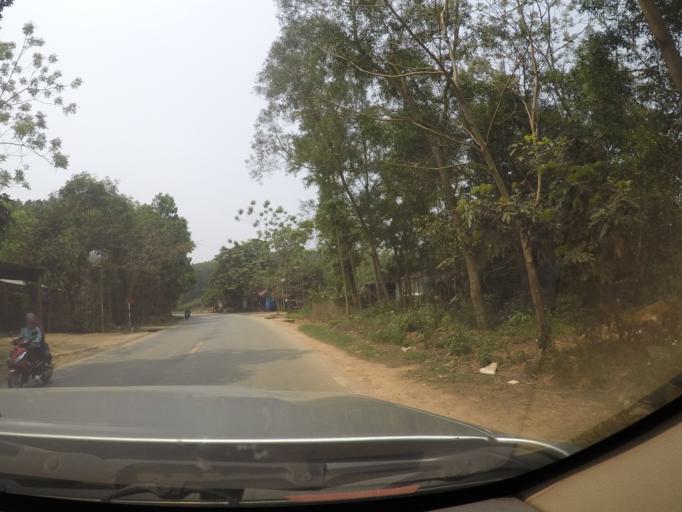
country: VN
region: Thanh Hoa
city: Thi Tran Ngoc Lac
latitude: 20.1254
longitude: 105.3908
